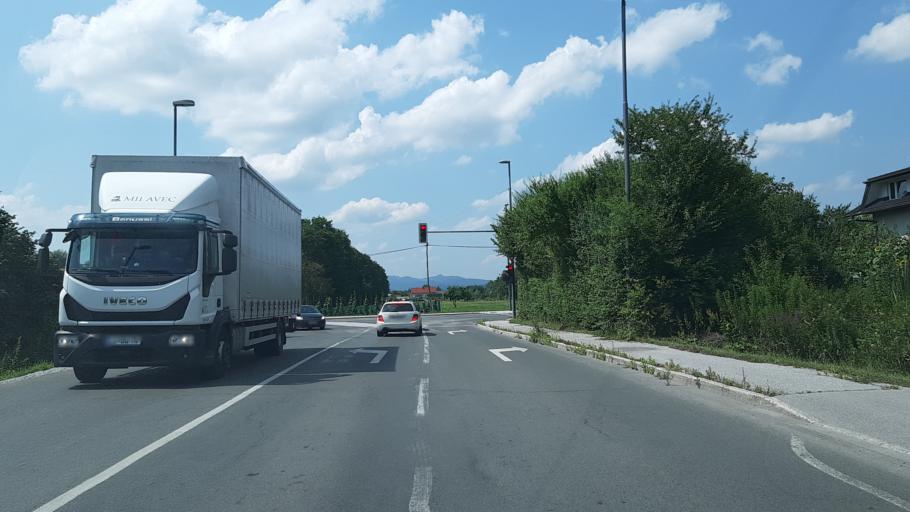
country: SI
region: Ljubljana
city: Ljubljana
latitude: 46.0200
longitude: 14.5223
